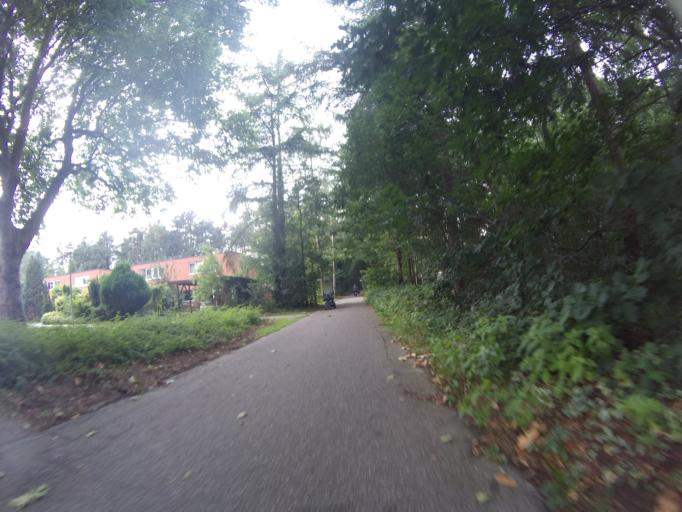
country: NL
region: Drenthe
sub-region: Gemeente Emmen
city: Emmen
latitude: 52.7841
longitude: 6.9175
